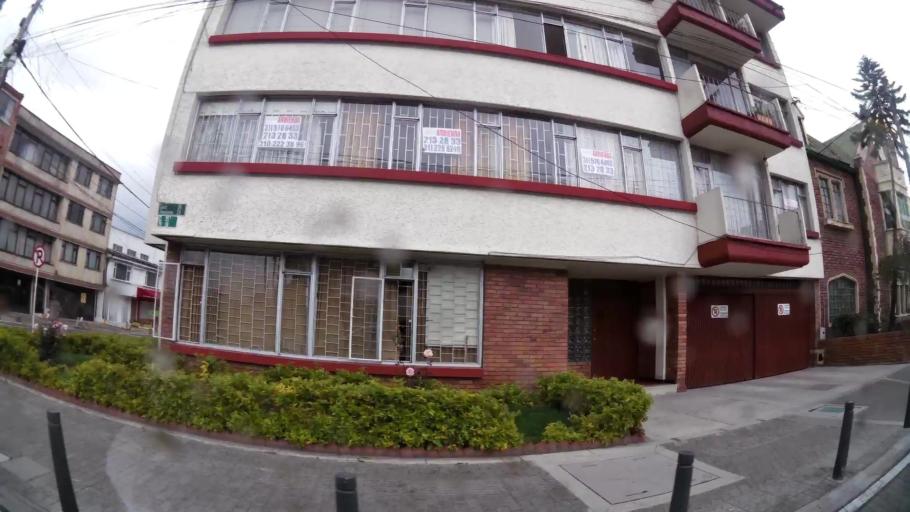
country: CO
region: Bogota D.C.
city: Bogota
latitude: 4.6251
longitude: -74.0787
